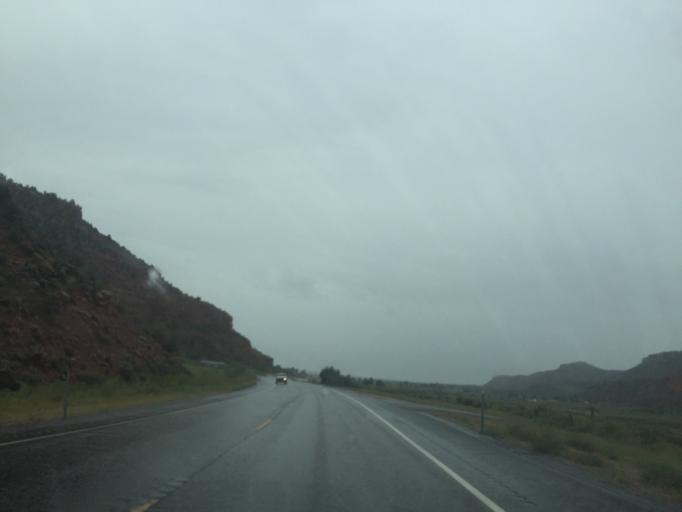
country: US
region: Utah
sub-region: Kane County
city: Kanab
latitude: 37.0662
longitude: -112.5370
